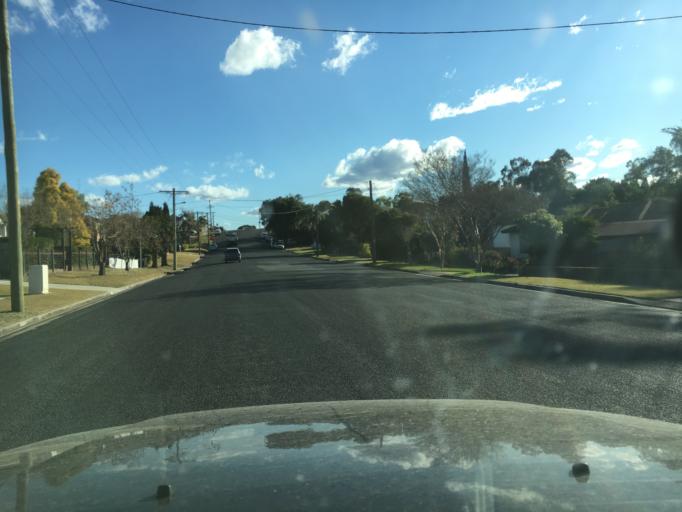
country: AU
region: New South Wales
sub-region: Maitland Municipality
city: East Maitland
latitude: -32.7538
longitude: 151.5834
